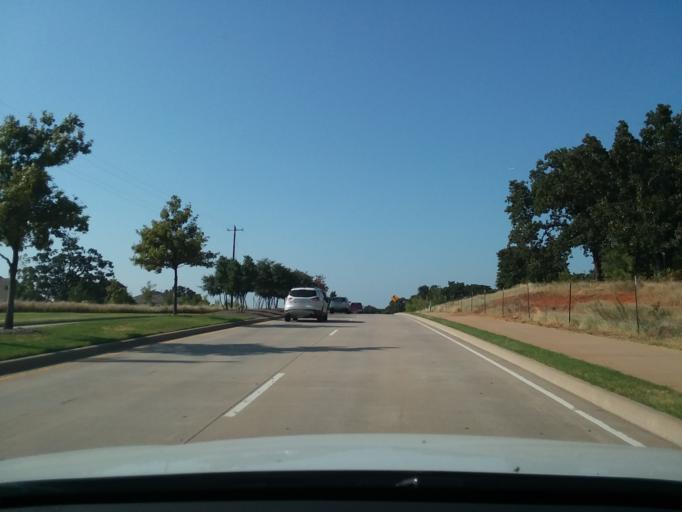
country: US
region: Texas
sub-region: Denton County
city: Flower Mound
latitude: 33.0374
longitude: -97.1053
